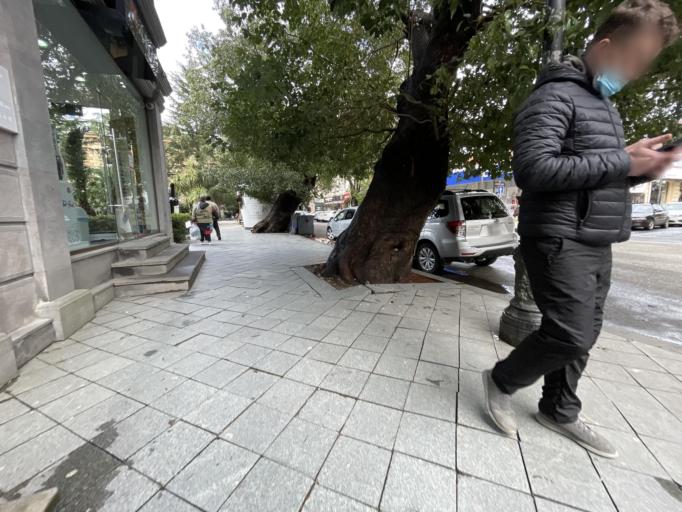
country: GE
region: Ajaria
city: Batumi
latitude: 41.6496
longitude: 41.6388
